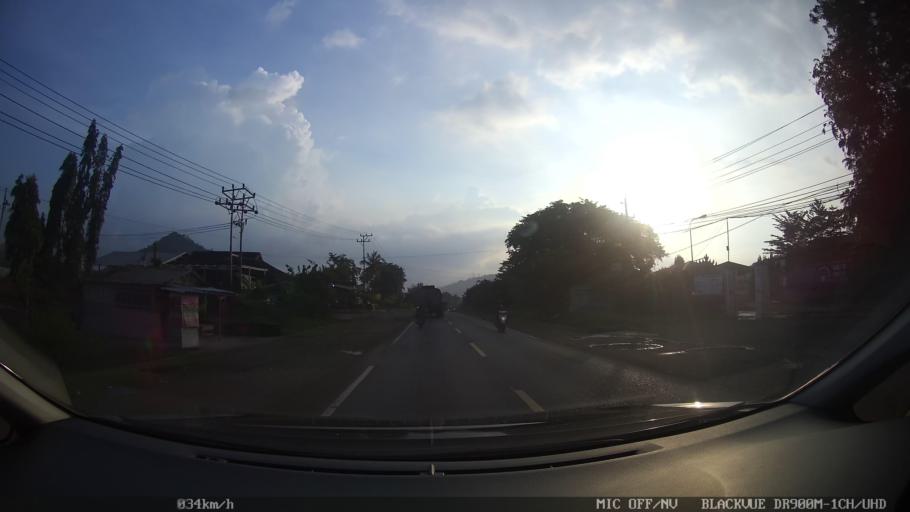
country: ID
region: Lampung
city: Panjang
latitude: -5.4181
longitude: 105.3415
